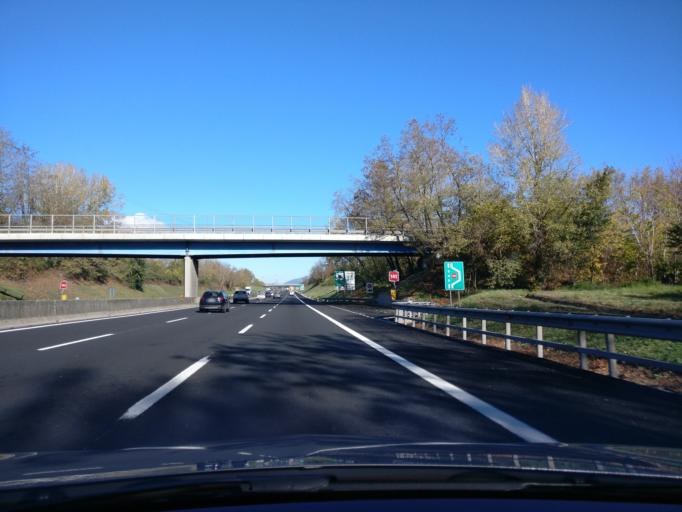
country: IT
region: Campania
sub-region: Provincia di Caserta
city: Zuni
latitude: 41.2244
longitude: 14.0968
